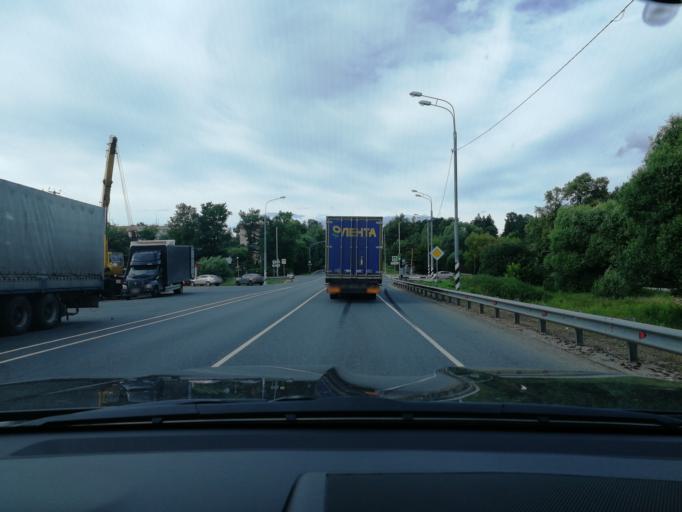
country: RU
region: Moskovskaya
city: Popovo
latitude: 55.0558
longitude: 37.7639
